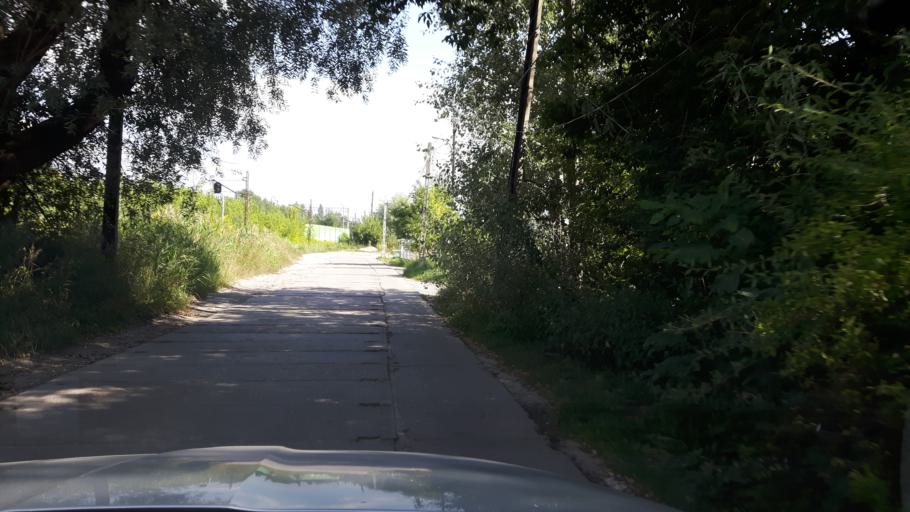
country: PL
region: Masovian Voivodeship
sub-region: Warszawa
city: Wlochy
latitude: 52.2093
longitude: 20.9363
